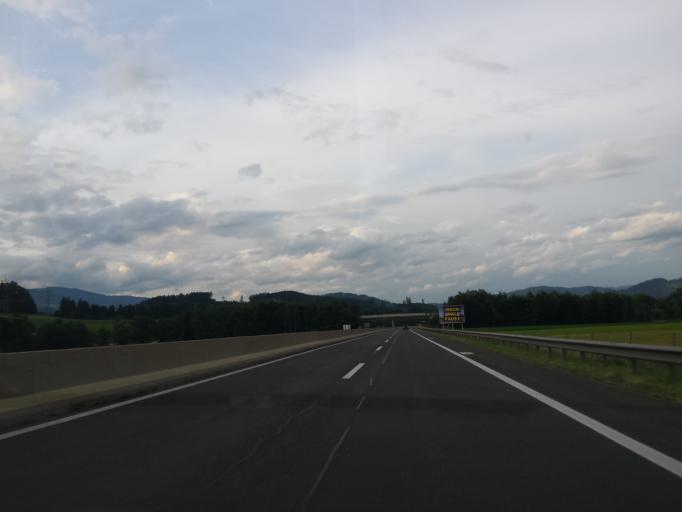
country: AT
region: Styria
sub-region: Politischer Bezirk Murtal
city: Kobenz
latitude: 47.2457
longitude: 14.8604
